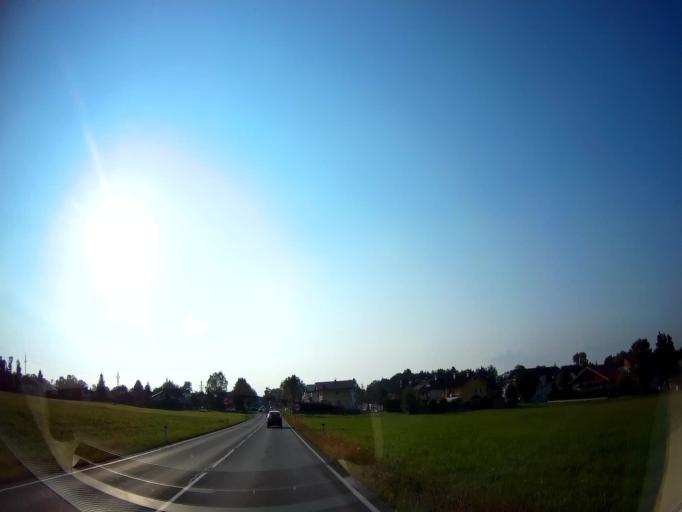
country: AT
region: Salzburg
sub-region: Politischer Bezirk Salzburg-Umgebung
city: Eugendorf
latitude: 47.8596
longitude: 13.1515
